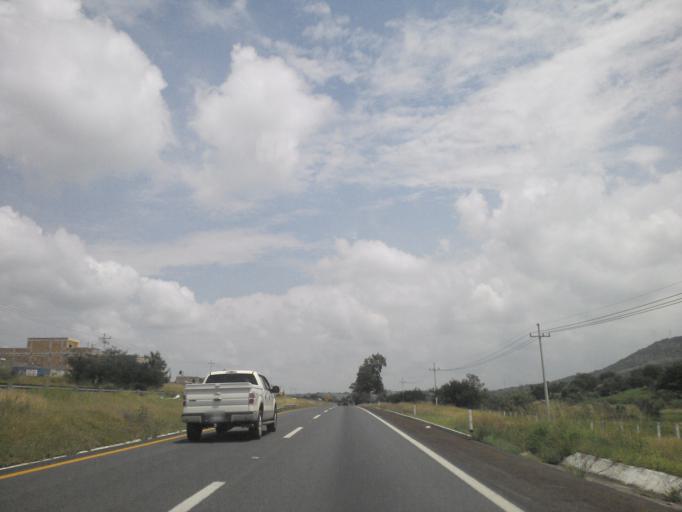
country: MX
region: Jalisco
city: Zapotlanejo
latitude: 20.6180
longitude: -103.0636
